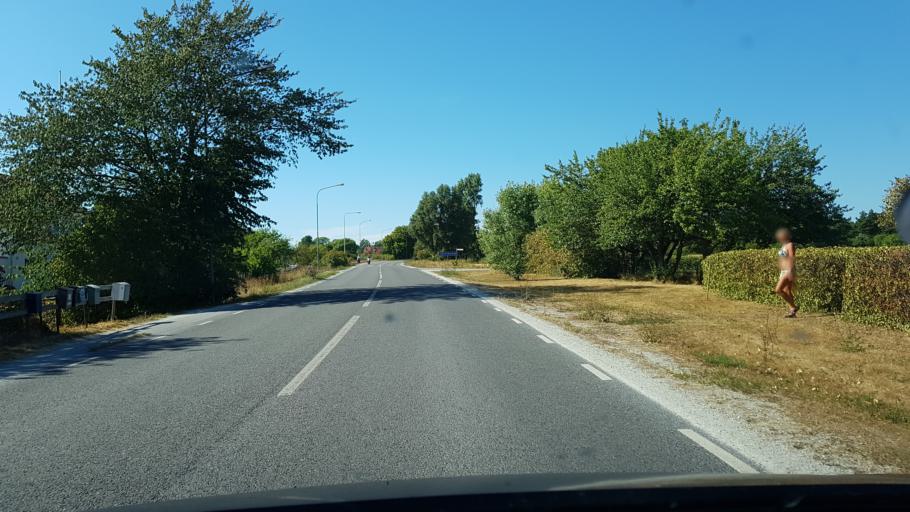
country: SE
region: Gotland
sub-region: Gotland
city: Klintehamn
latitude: 57.4318
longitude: 18.1483
